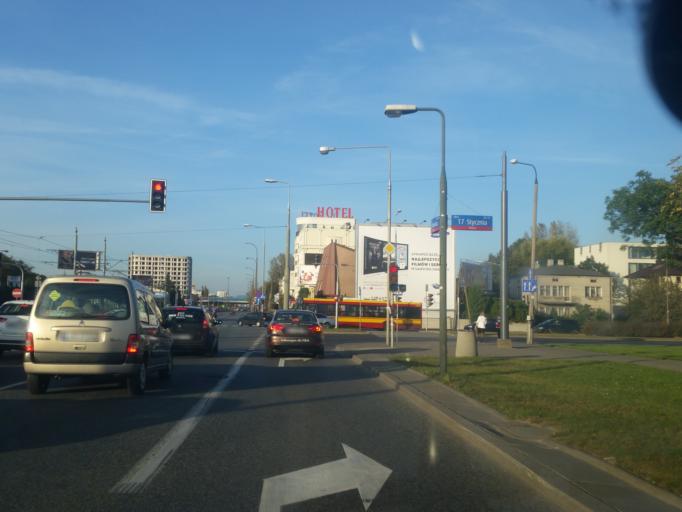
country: PL
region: Masovian Voivodeship
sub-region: Warszawa
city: Wlochy
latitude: 52.1854
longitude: 20.9542
